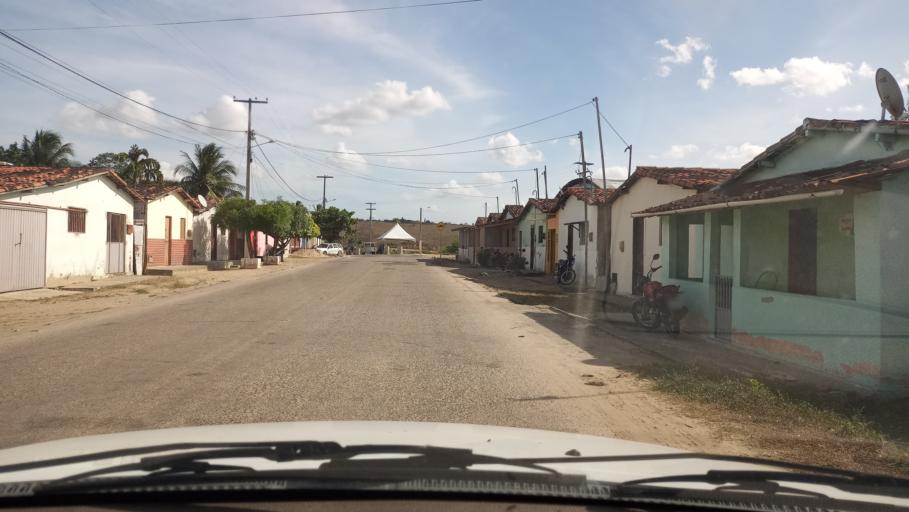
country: BR
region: Rio Grande do Norte
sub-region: Goianinha
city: Goianinha
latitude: -6.3297
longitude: -35.3041
